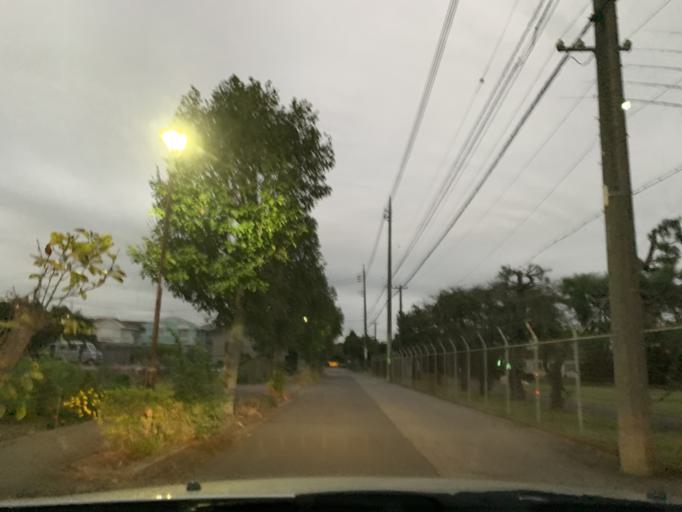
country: JP
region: Chiba
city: Nagareyama
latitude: 35.8889
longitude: 139.9363
